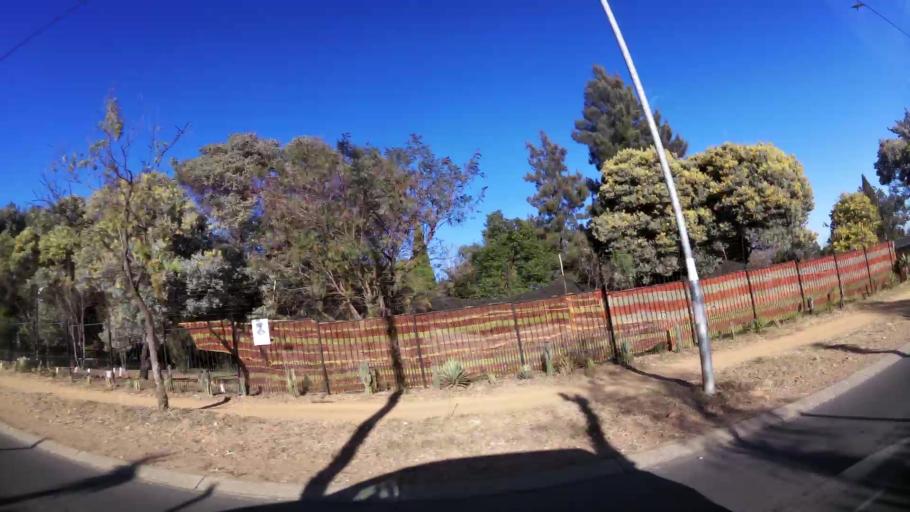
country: ZA
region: Gauteng
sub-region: City of Johannesburg Metropolitan Municipality
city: Midrand
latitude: -26.0232
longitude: 28.1466
